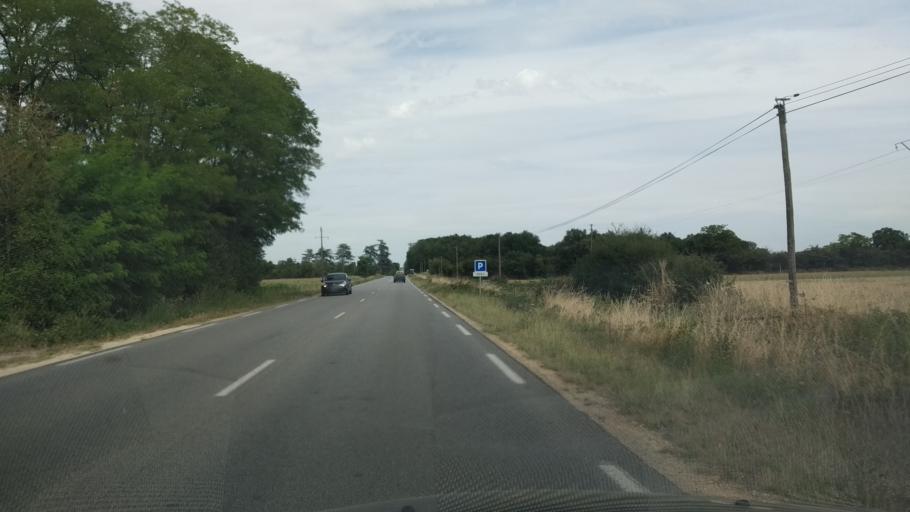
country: FR
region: Poitou-Charentes
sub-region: Departement de la Vienne
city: Mignaloux-Beauvoir
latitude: 46.5629
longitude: 0.4150
